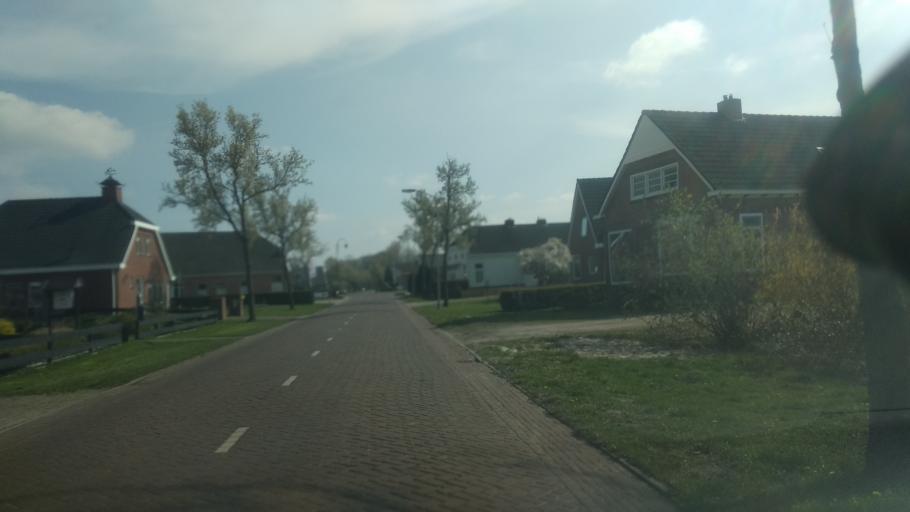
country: NL
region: Drenthe
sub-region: Gemeente Borger-Odoorn
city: Borger
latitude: 52.9356
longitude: 6.8799
